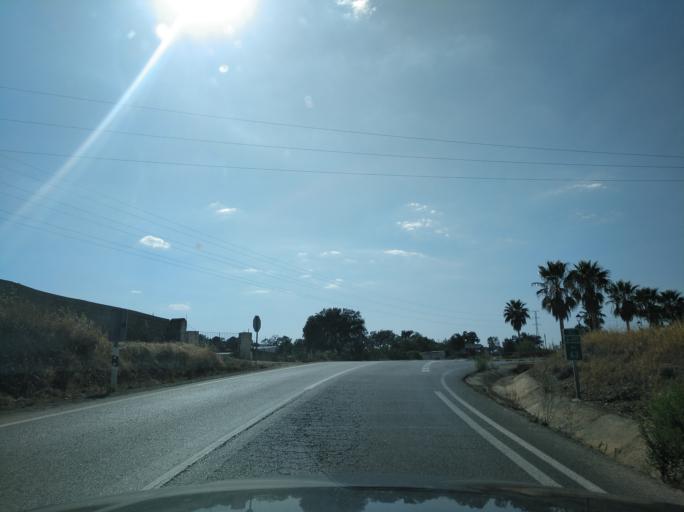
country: ES
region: Andalusia
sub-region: Provincia de Huelva
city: Santa Barbara de Casa
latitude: 37.7920
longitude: -7.1851
